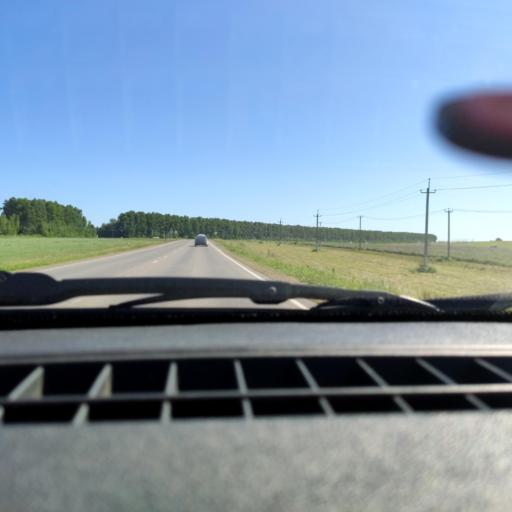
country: RU
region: Bashkortostan
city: Iglino
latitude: 54.8757
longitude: 56.4693
